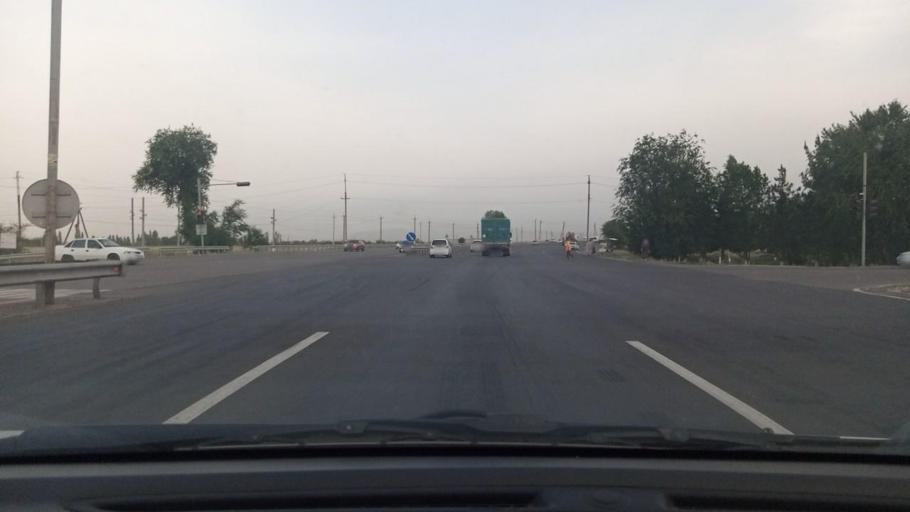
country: UZ
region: Toshkent
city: Ohangaron
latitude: 40.9302
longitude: 69.5951
